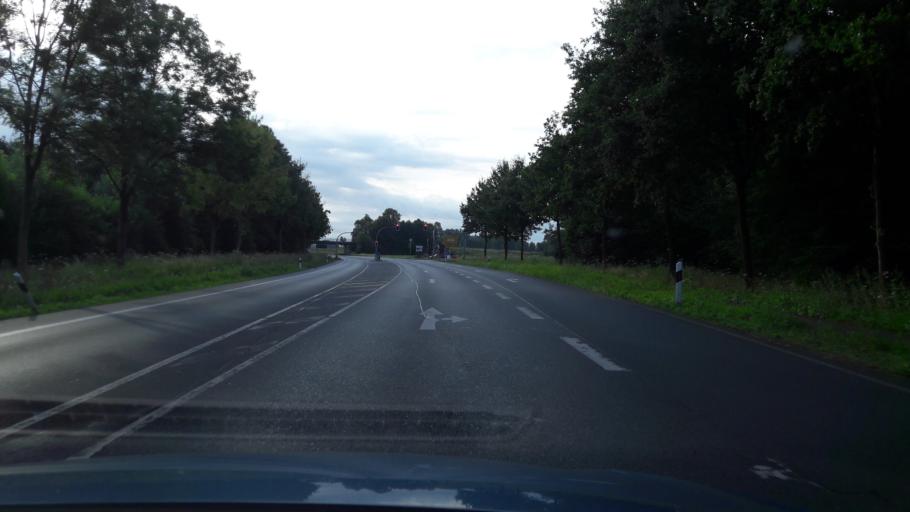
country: DE
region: North Rhine-Westphalia
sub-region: Regierungsbezirk Munster
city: Telgte
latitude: 51.9385
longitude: 7.7106
